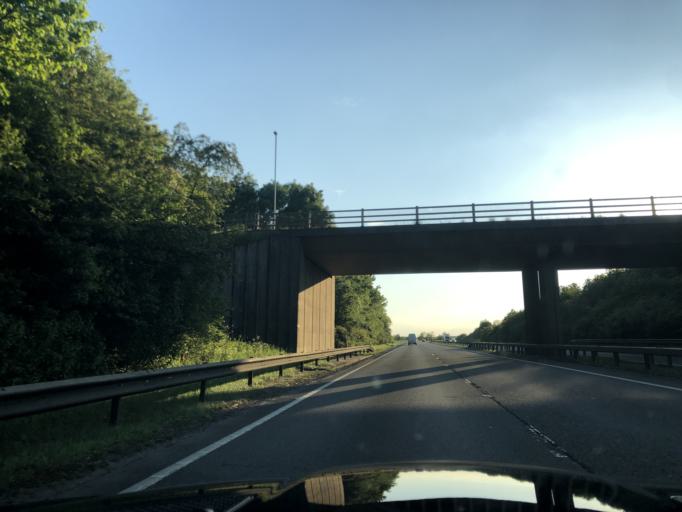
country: GB
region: England
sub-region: Northamptonshire
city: Thrapston
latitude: 52.3908
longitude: -0.5566
